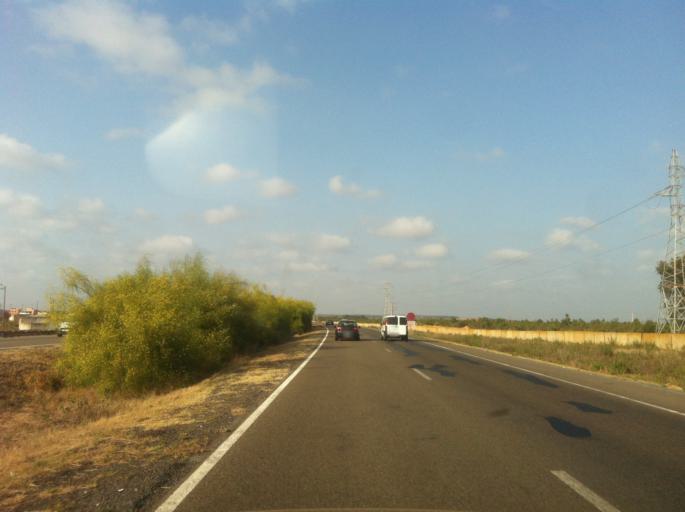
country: MA
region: Gharb-Chrarda-Beni Hssen
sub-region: Kenitra Province
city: Kenitra
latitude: 34.2299
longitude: -6.5722
